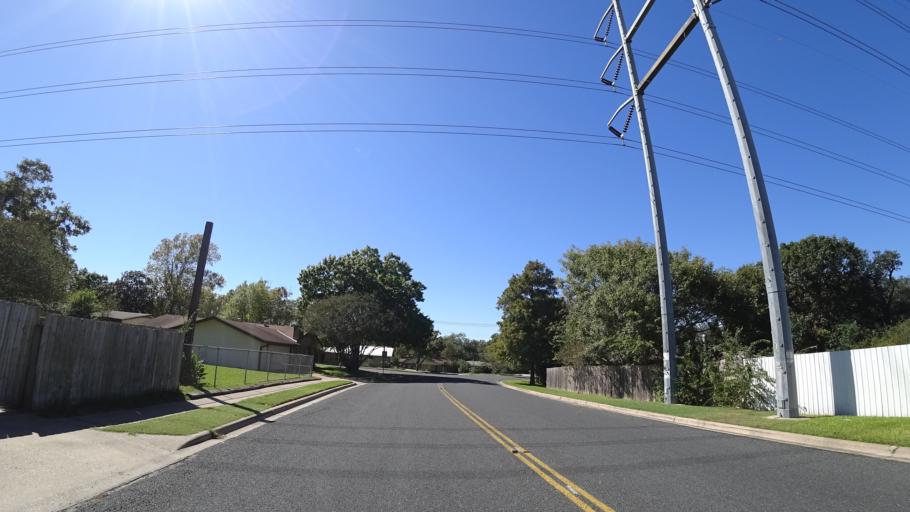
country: US
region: Texas
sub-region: Travis County
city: Rollingwood
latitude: 30.2280
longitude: -97.7947
